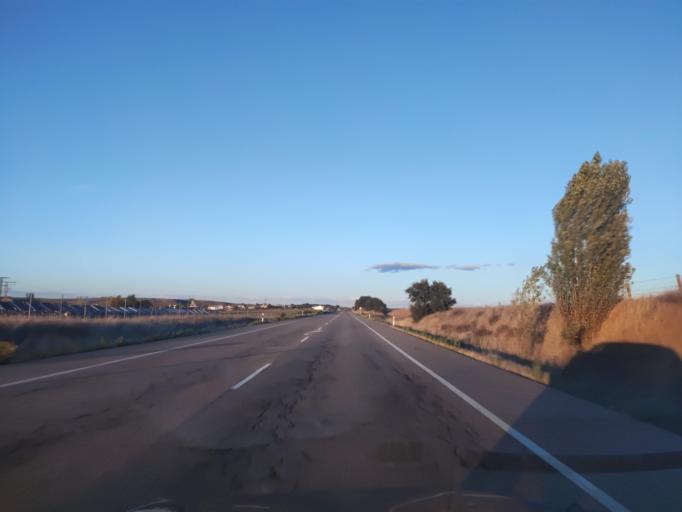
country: ES
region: Castille and Leon
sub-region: Provincia de Salamanca
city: Martin de Yeltes
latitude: 40.7700
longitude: -6.3001
